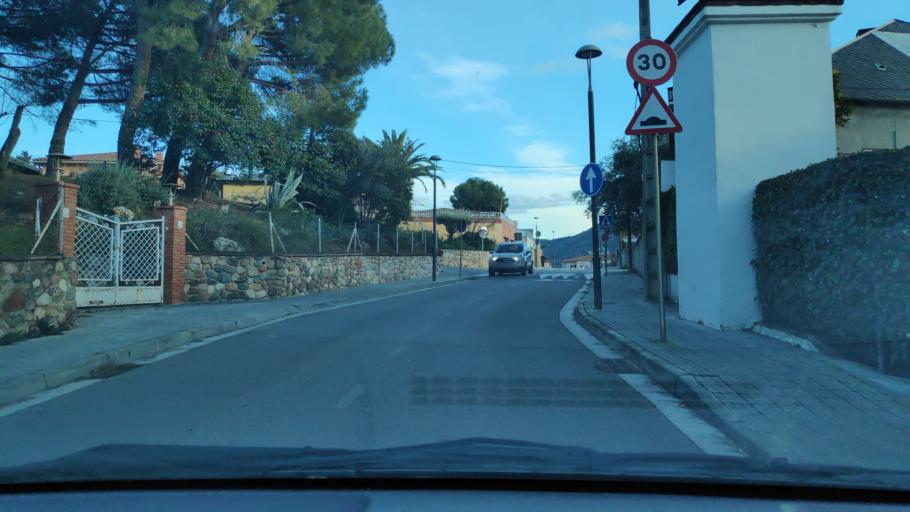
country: ES
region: Catalonia
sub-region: Provincia de Barcelona
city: Montmelo
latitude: 41.5540
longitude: 2.2453
